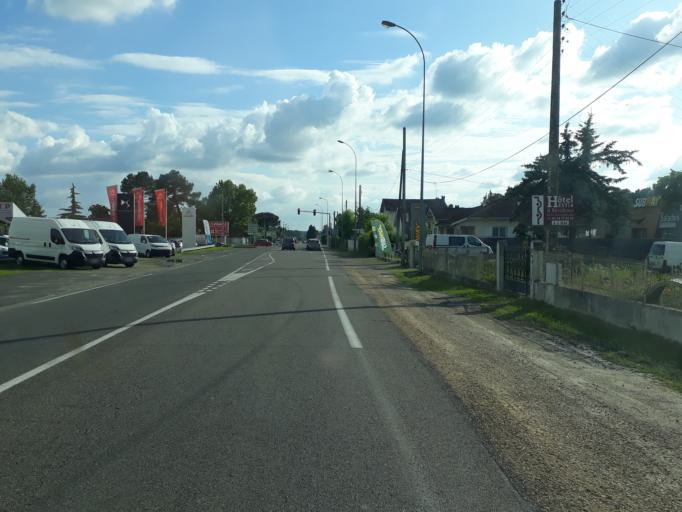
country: FR
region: Aquitaine
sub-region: Departement des Landes
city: Mont-de-Marsan
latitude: 43.9071
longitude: -0.4715
